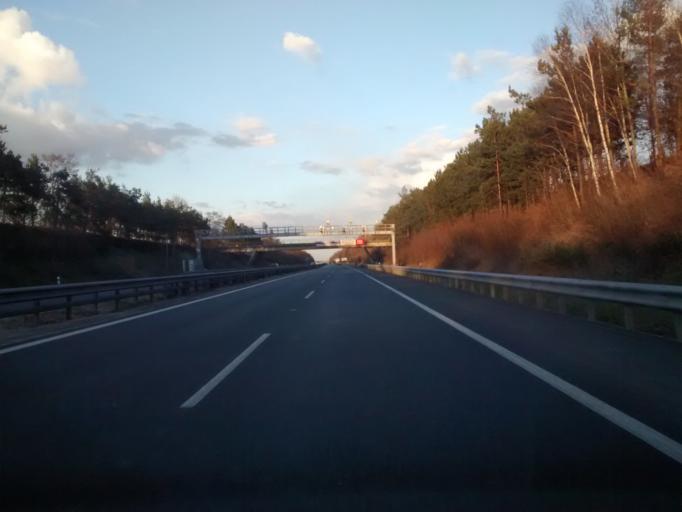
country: CZ
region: Central Bohemia
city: Nehvizdy
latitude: 50.1255
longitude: 14.7290
